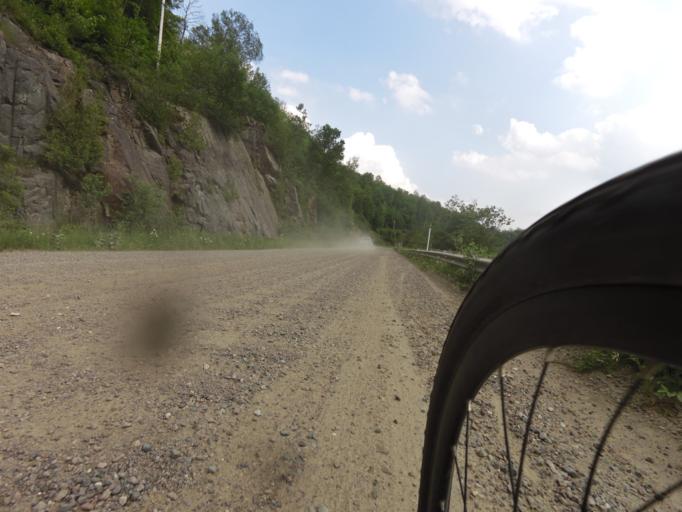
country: CA
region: Quebec
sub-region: Laurentides
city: Brownsburg-Chatham
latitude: 45.9150
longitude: -74.5983
